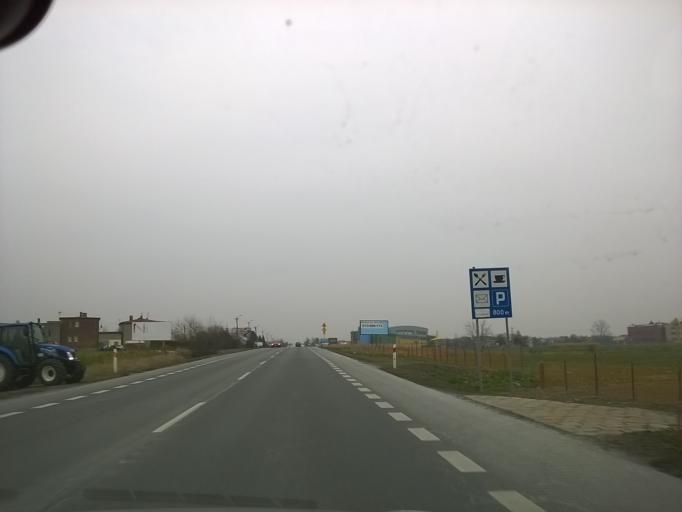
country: PL
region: Silesian Voivodeship
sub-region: Powiat gliwicki
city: Paniowki
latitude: 50.2370
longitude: 18.7775
